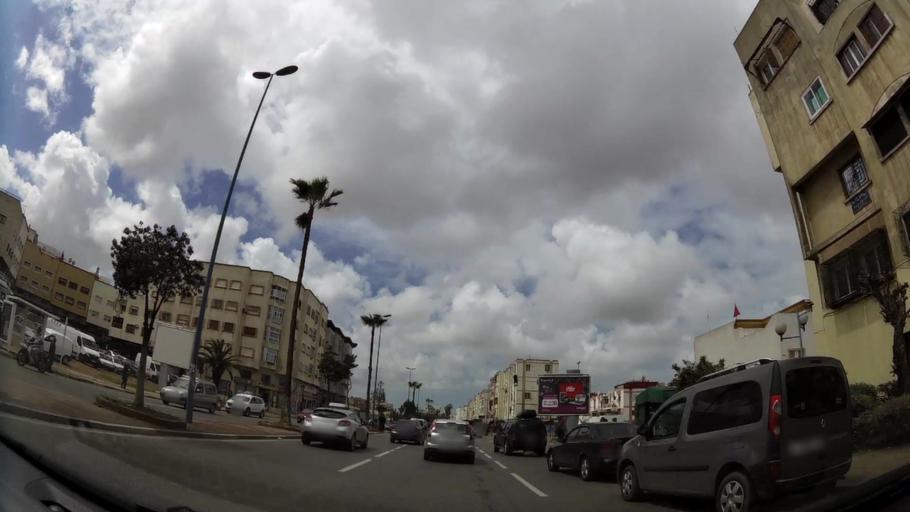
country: MA
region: Grand Casablanca
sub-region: Casablanca
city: Casablanca
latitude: 33.5415
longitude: -7.5930
